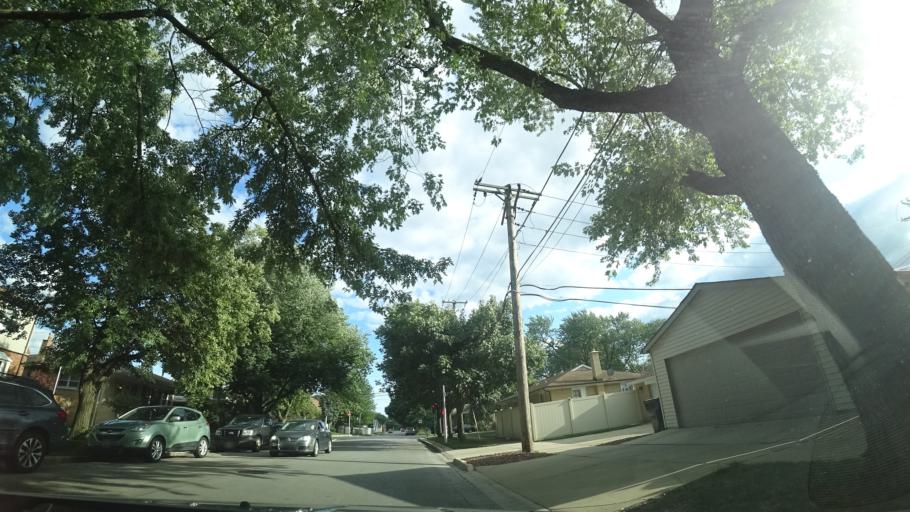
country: US
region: Illinois
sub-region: Cook County
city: Merrionette Park
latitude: 41.6848
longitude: -87.7103
